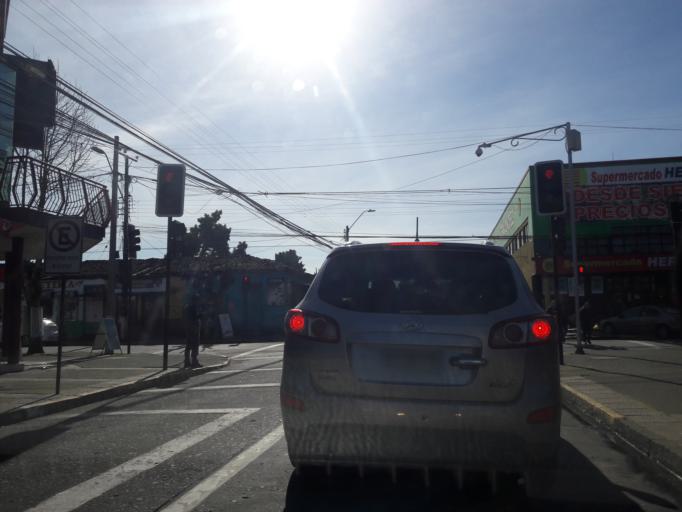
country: CL
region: Biobio
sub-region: Provincia de Biobio
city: Cabrero
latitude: -37.0348
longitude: -72.4032
